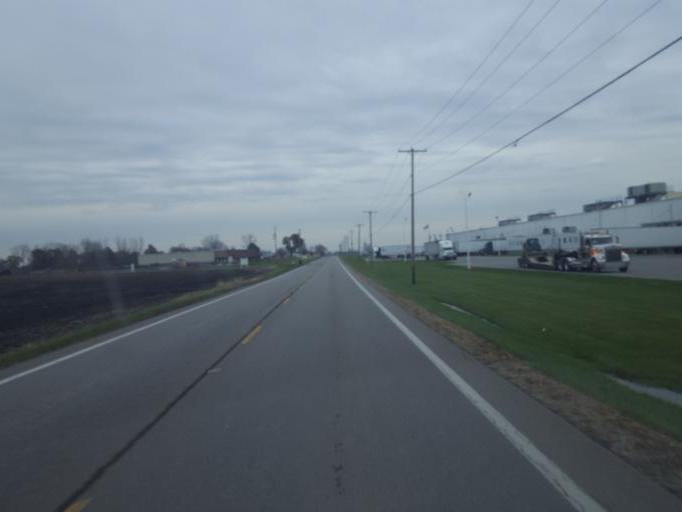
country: US
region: Ohio
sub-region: Marion County
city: Marion
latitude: 40.6114
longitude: -83.0410
